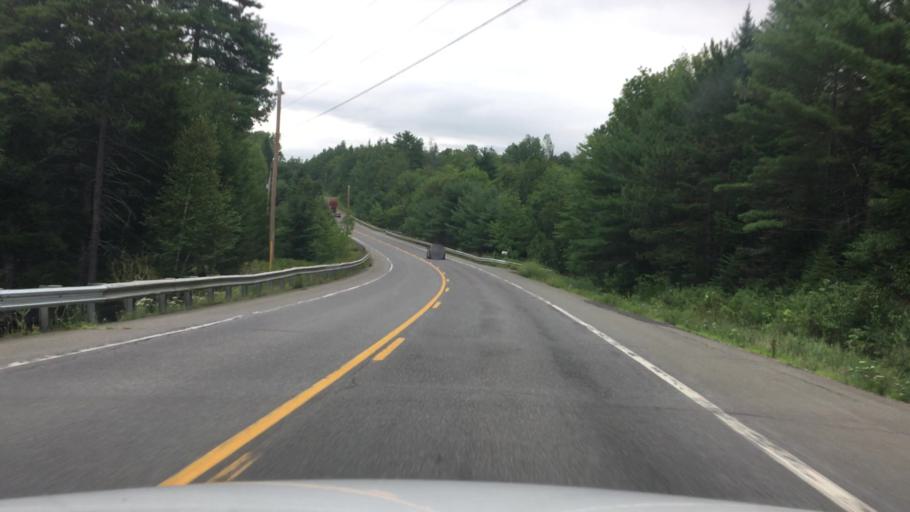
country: US
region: Maine
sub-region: Penobscot County
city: Bradley
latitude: 44.8245
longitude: -68.4078
